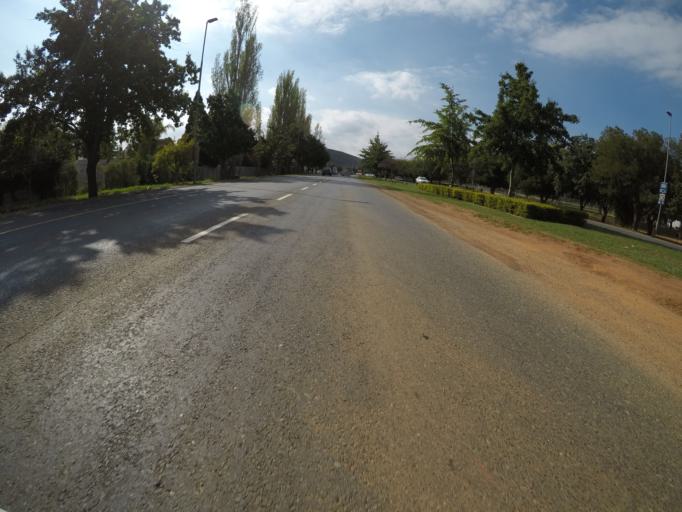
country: ZA
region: Western Cape
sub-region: Cape Winelands District Municipality
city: Stellenbosch
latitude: -33.9462
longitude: 18.8532
